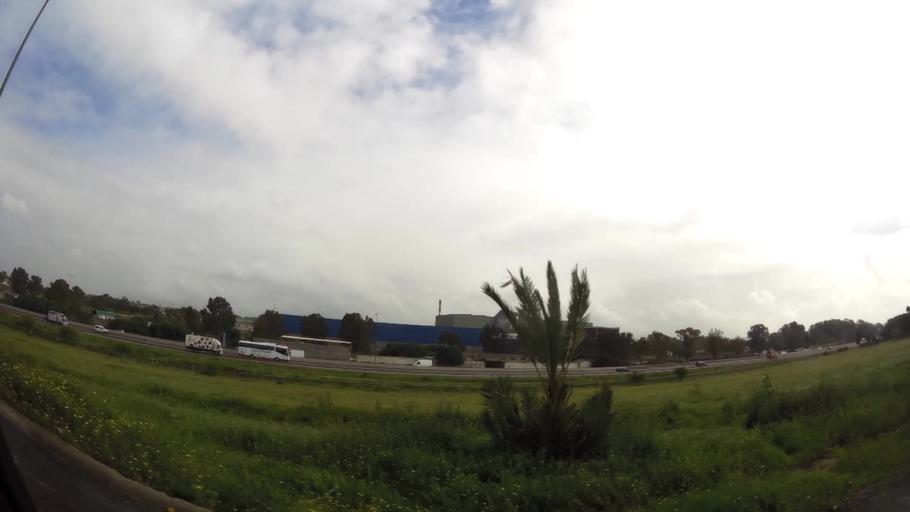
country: MA
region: Grand Casablanca
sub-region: Mohammedia
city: Mohammedia
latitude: 33.6412
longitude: -7.4362
